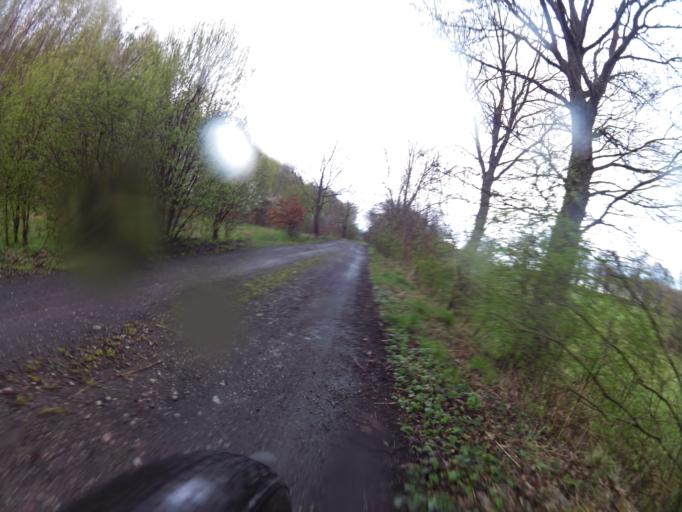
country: PL
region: Pomeranian Voivodeship
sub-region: Powiat slupski
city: Kepice
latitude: 54.2747
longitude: 16.7964
